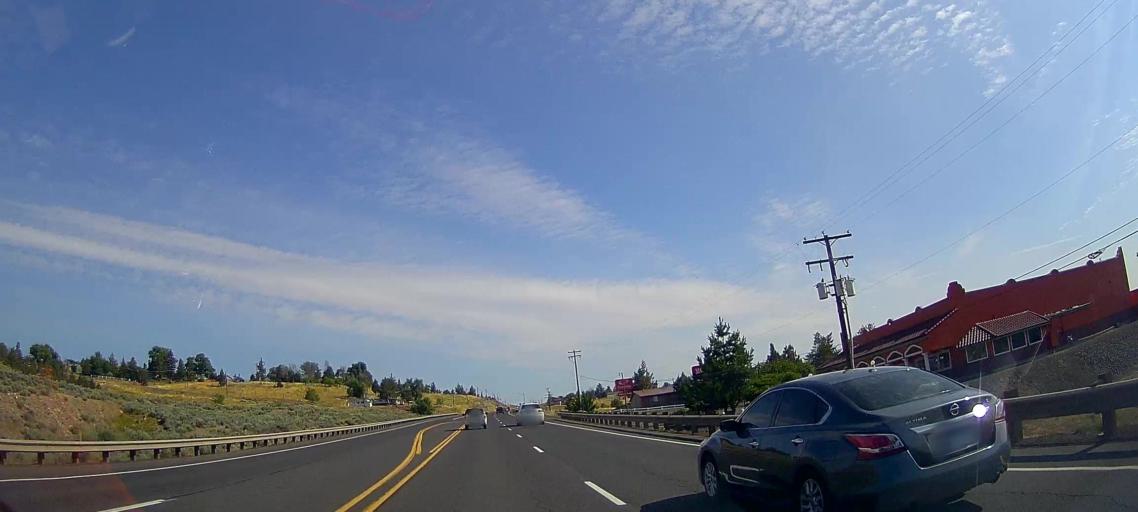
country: US
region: Oregon
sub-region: Jefferson County
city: Madras
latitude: 44.6446
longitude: -121.1295
